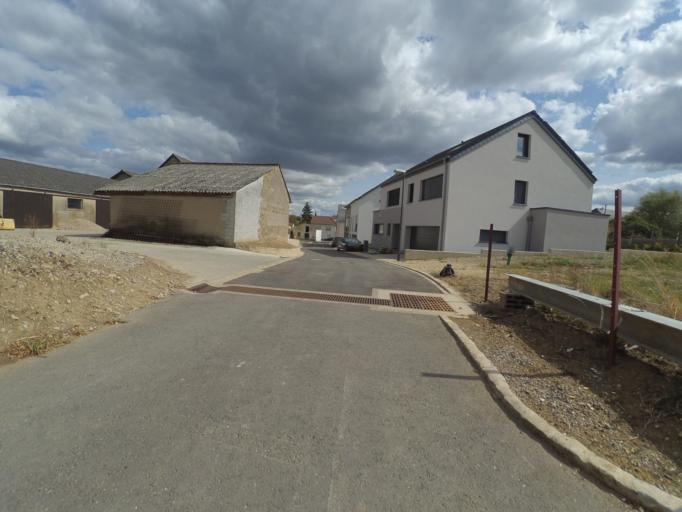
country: LU
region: Grevenmacher
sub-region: Canton de Remich
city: Mondorf-les-Bains
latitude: 49.5215
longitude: 6.2966
